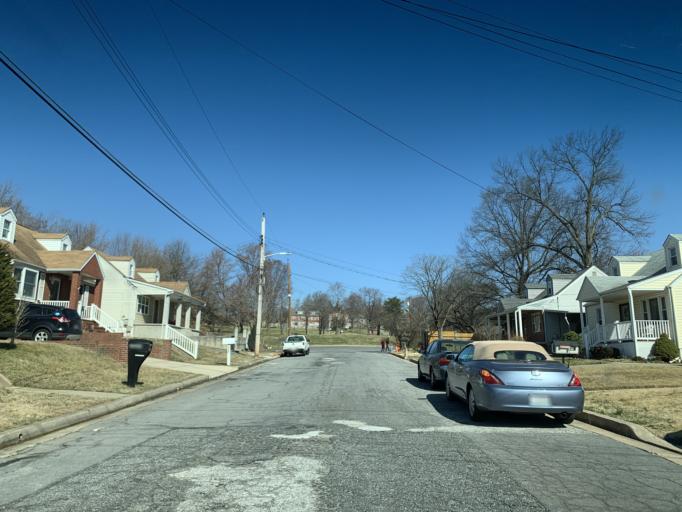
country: US
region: Maryland
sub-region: Baltimore County
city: Rossville
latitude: 39.3292
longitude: -76.4970
